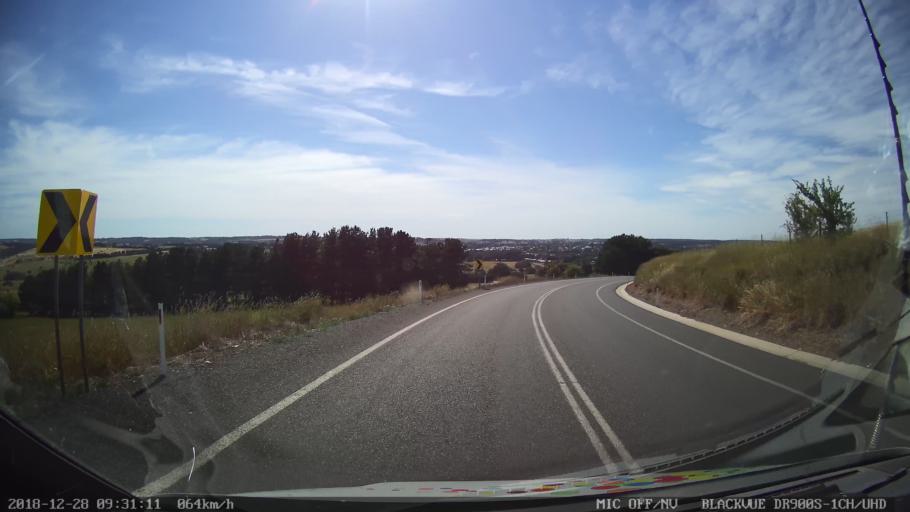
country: AU
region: New South Wales
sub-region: Upper Lachlan Shire
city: Crookwell
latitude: -34.4499
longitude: 149.4449
